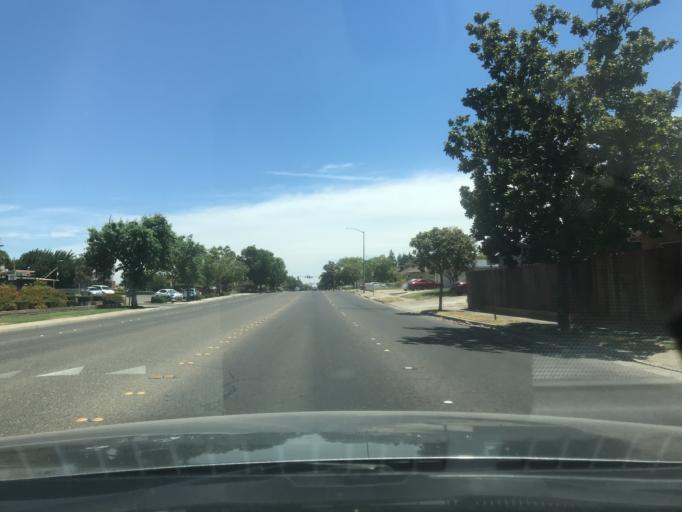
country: US
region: California
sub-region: Merced County
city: Atwater
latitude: 37.3604
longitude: -120.6073
